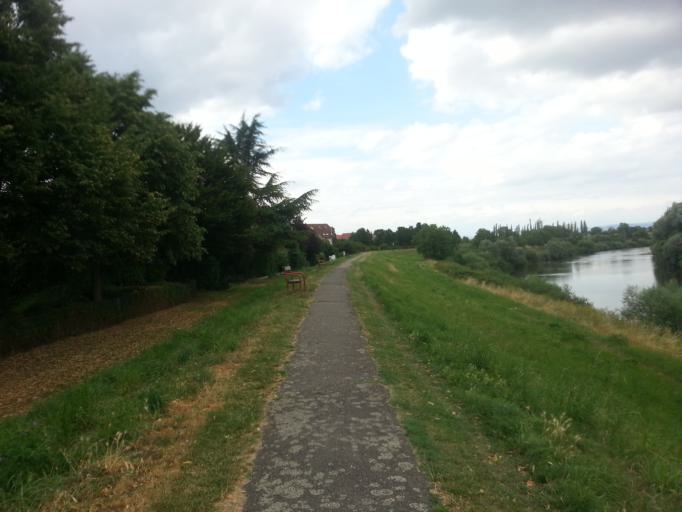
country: DE
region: Baden-Wuerttemberg
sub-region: Karlsruhe Region
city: Ilvesheim
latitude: 49.4726
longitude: 8.5724
